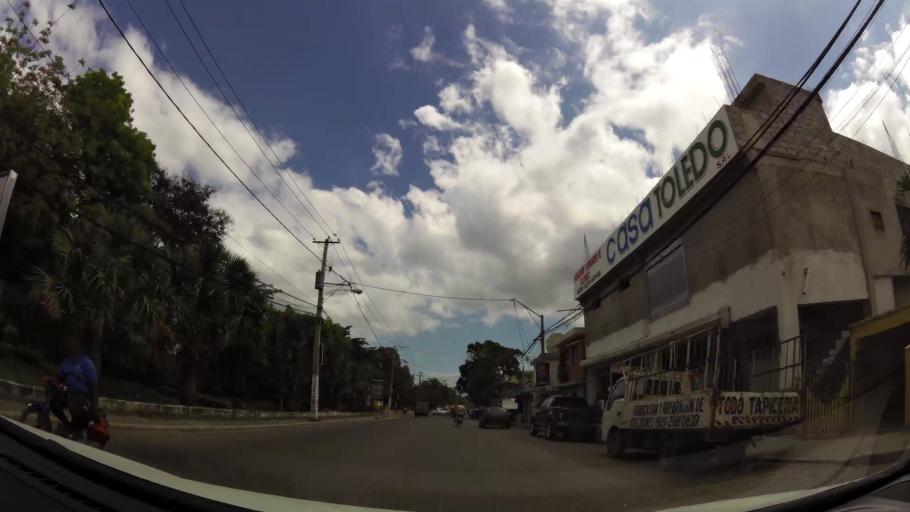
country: DO
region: San Cristobal
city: San Cristobal
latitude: 18.4139
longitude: -70.1182
